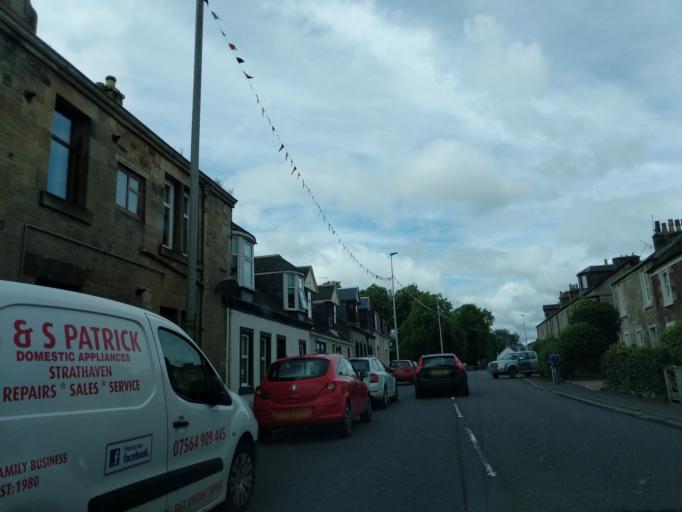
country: GB
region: Scotland
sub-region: South Lanarkshire
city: Strathaven
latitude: 55.6805
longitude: -4.0679
